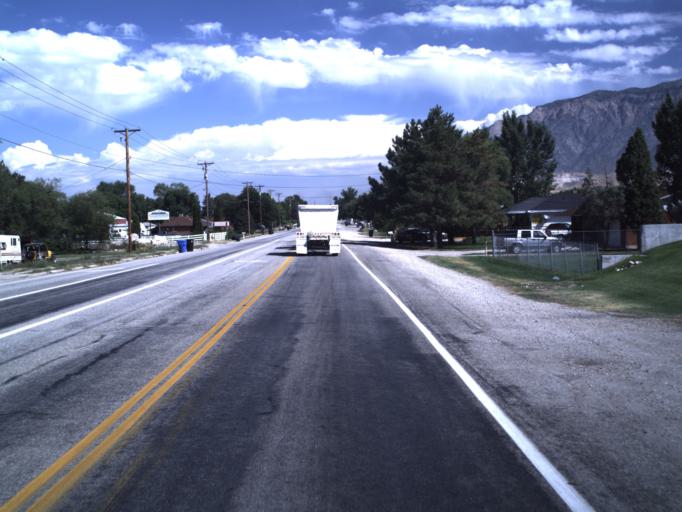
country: US
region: Utah
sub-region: Weber County
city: Farr West
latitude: 41.2898
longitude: -112.0278
